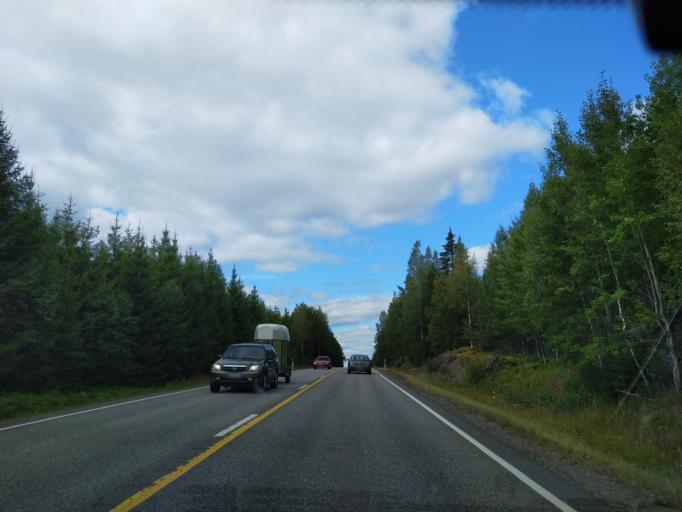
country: FI
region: Haeme
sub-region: Riihimaeki
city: Loppi
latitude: 60.7452
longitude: 24.3468
